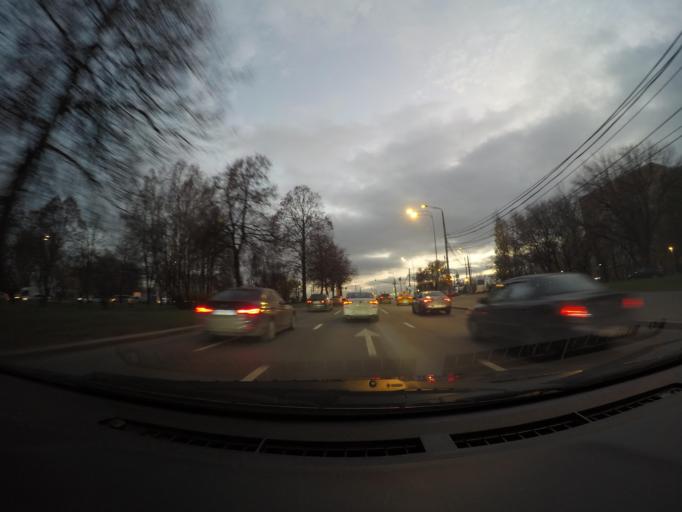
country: RU
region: Moscow
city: Kolomenskoye
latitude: 55.6689
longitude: 37.6612
